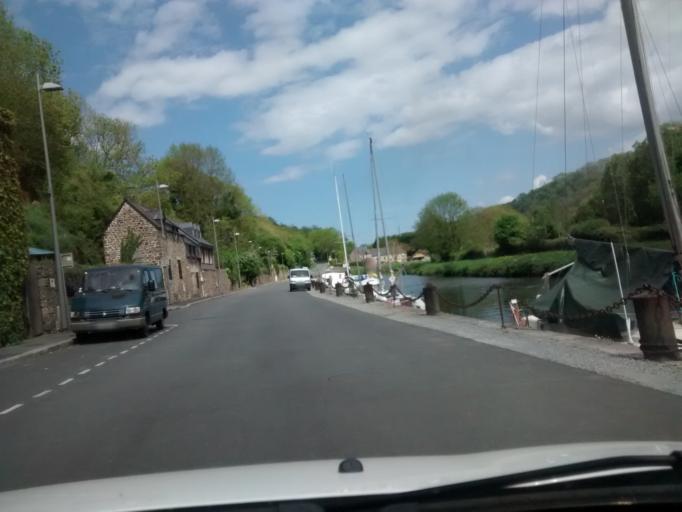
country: FR
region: Brittany
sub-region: Departement des Cotes-d'Armor
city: Lanvallay
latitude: 48.4599
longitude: -2.0351
